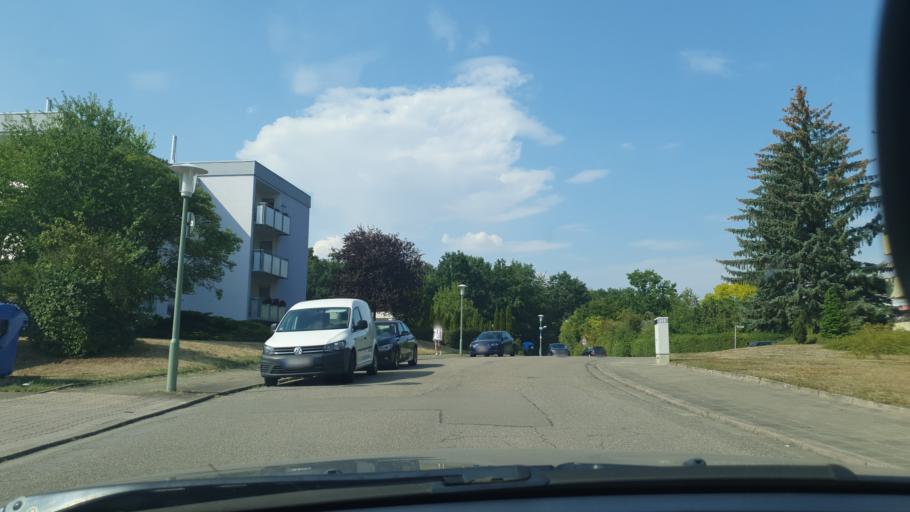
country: DE
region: Rheinland-Pfalz
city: Stelzenberg
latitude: 49.4294
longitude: 7.7269
